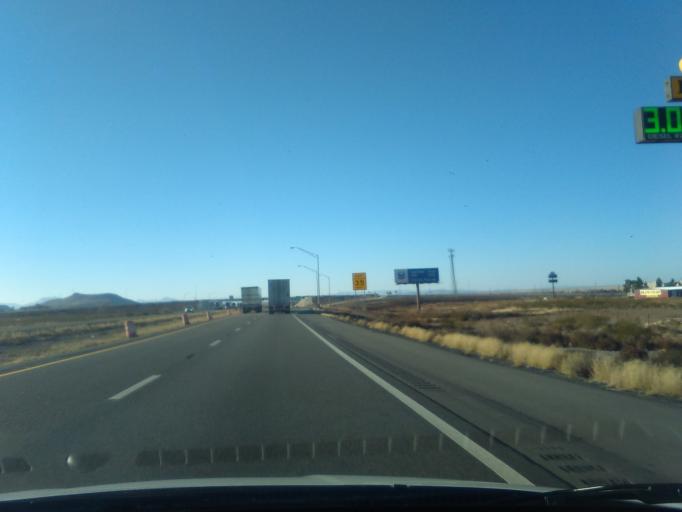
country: US
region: New Mexico
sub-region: Hidalgo County
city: Lordsburg
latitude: 32.3510
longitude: -108.7356
